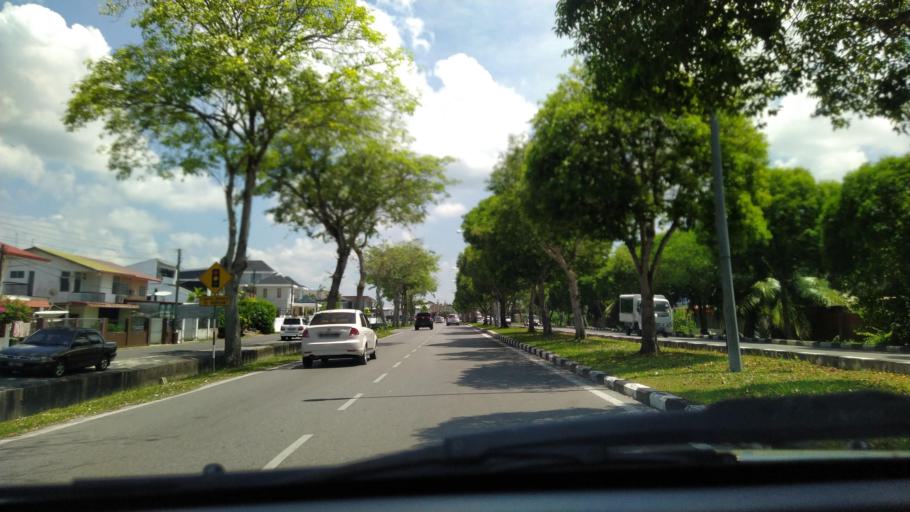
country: MY
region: Sarawak
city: Sibu
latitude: 2.3049
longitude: 111.8302
